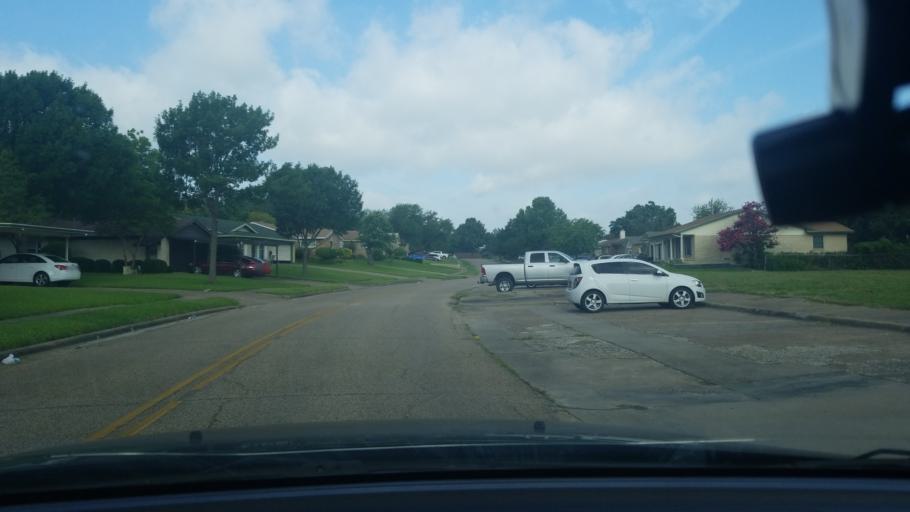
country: US
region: Texas
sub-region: Dallas County
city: Mesquite
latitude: 32.7734
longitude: -96.6324
